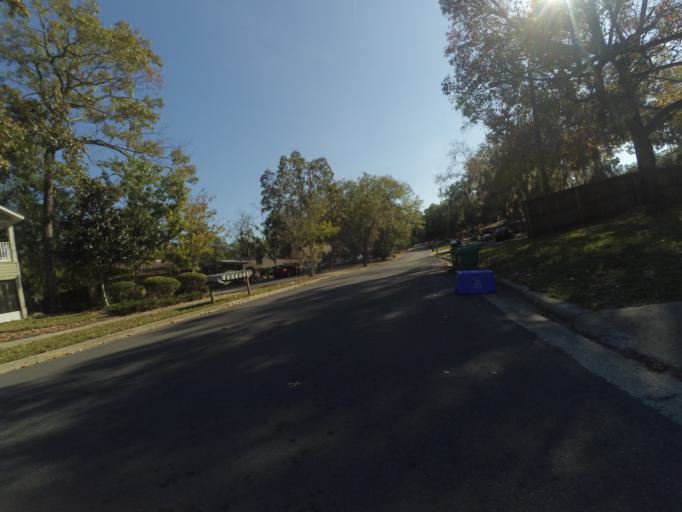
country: US
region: Florida
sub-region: Alachua County
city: Gainesville
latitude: 29.6188
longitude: -82.3667
